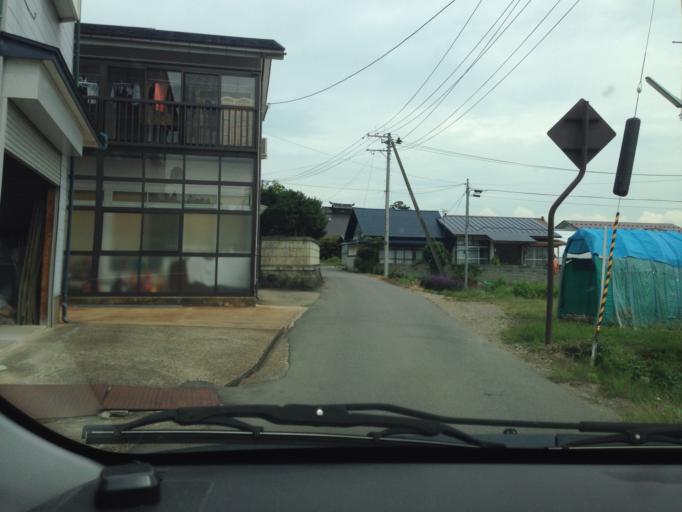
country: JP
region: Fukushima
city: Kitakata
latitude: 37.5615
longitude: 139.8006
